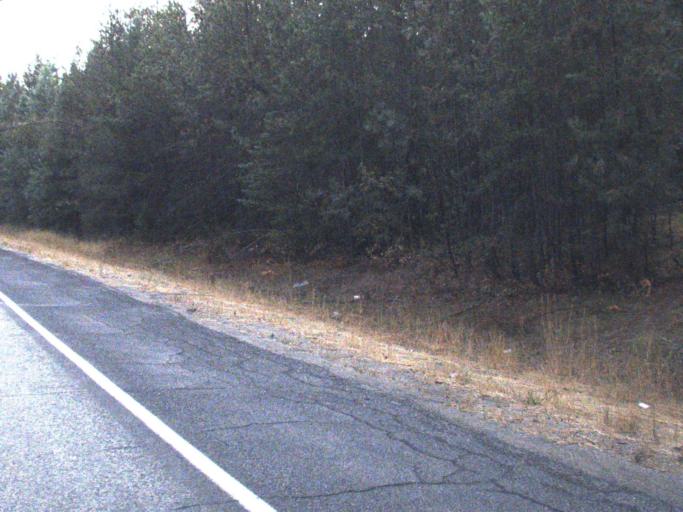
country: US
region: Washington
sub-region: Stevens County
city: Chewelah
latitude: 48.0603
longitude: -117.7297
